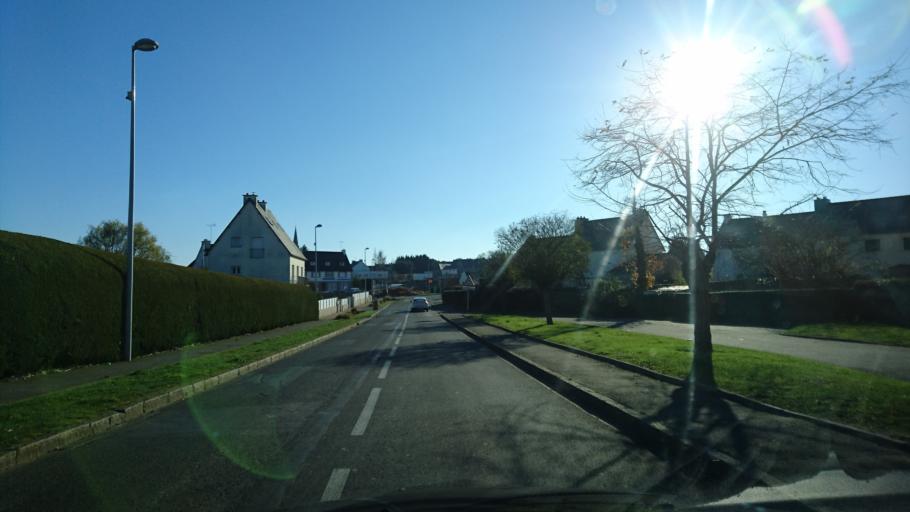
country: FR
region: Brittany
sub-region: Departement des Cotes-d'Armor
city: Pledran
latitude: 48.4486
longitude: -2.7478
